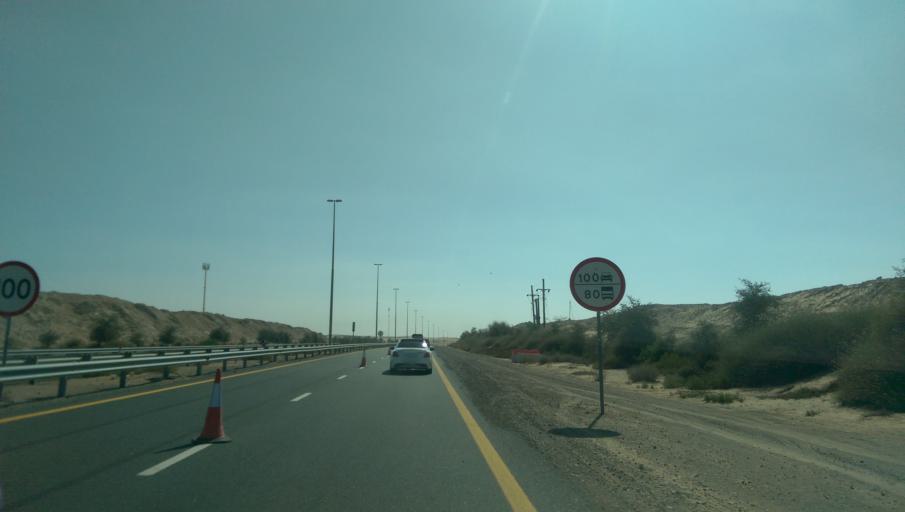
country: AE
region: Dubai
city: Dubai
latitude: 24.9885
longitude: 55.3217
